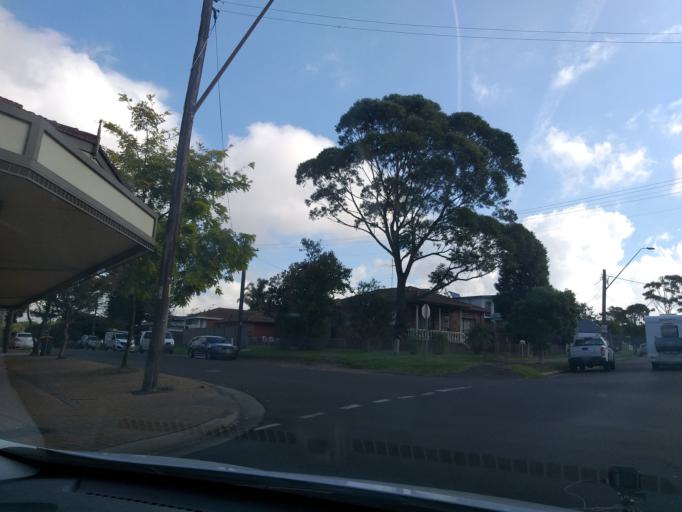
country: AU
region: New South Wales
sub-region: Wollongong
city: Helensburgh
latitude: -34.1910
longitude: 150.9806
